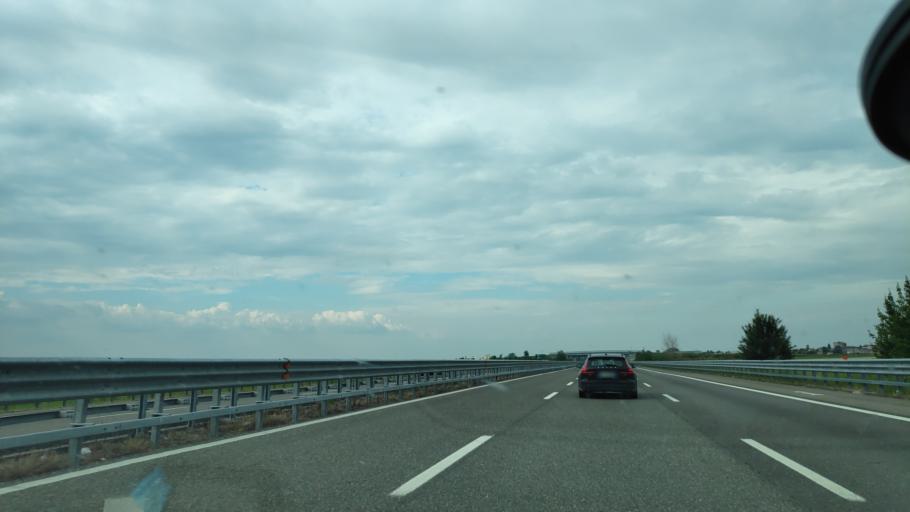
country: IT
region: Lombardy
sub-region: Provincia di Pavia
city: Silvano Pietra
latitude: 45.0296
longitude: 8.9347
